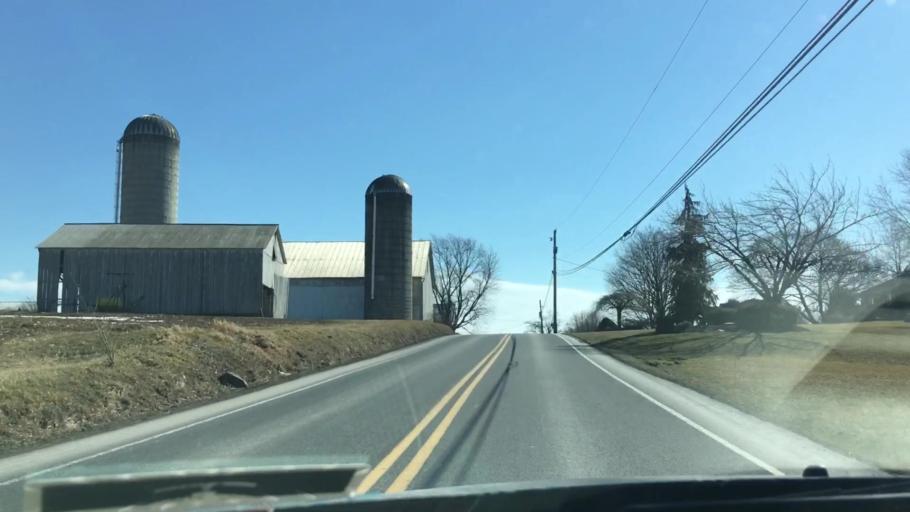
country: US
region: Pennsylvania
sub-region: Lancaster County
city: Reamstown
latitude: 40.1757
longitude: -76.1268
